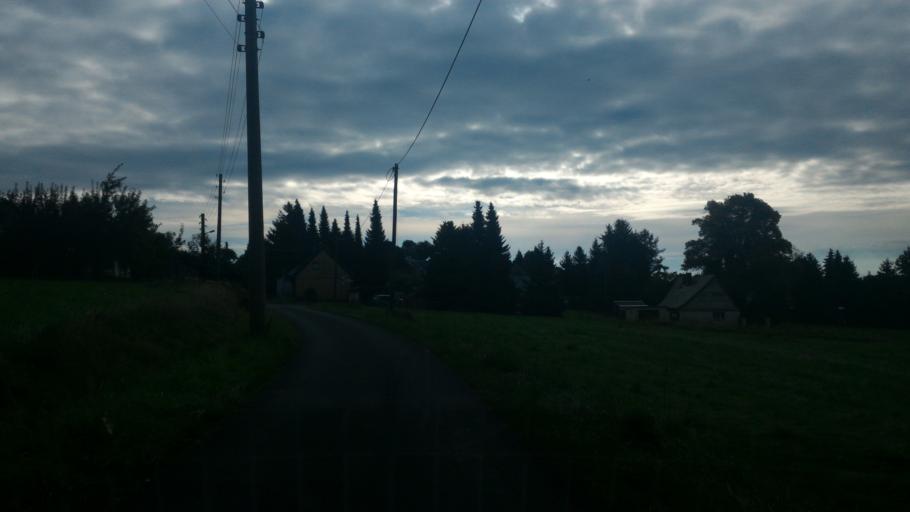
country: DE
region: Saxony
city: Leutersdorf
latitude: 50.9561
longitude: 14.6258
